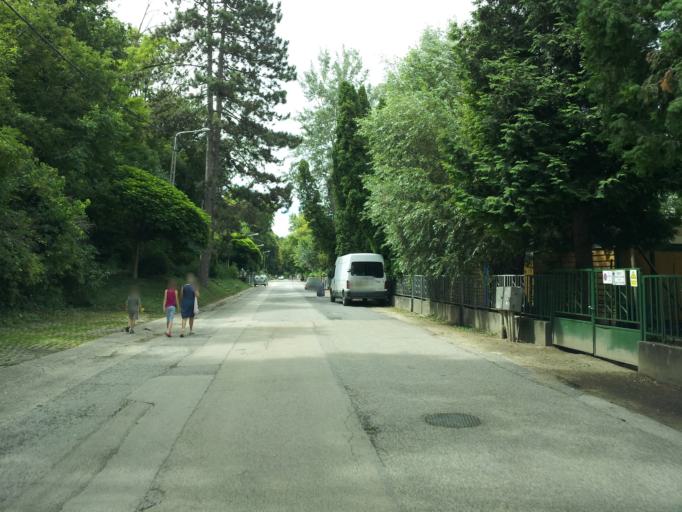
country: HU
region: Somogy
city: Balatonszabadi
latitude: 46.9672
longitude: 18.1590
